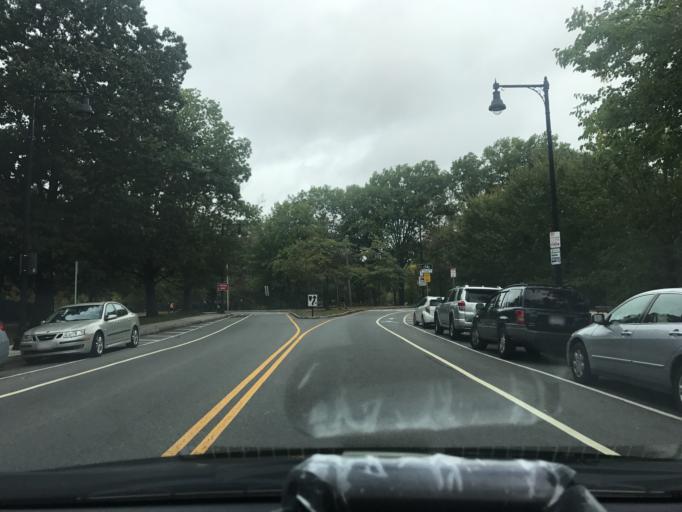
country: US
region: Massachusetts
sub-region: Norfolk County
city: Brookline
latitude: 42.3402
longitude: -71.0931
